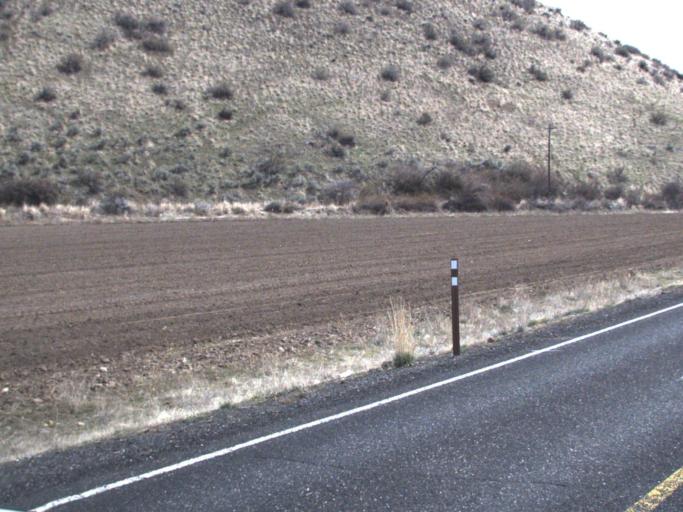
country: US
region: Washington
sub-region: Yakima County
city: Tieton
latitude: 46.7798
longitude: -120.8628
